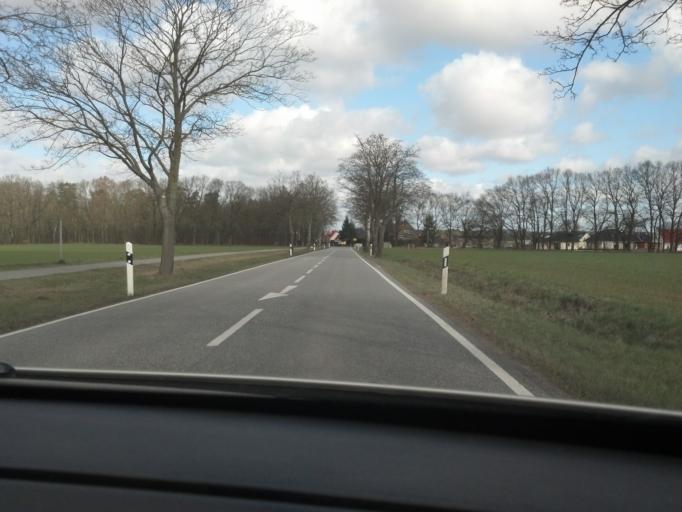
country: DE
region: Mecklenburg-Vorpommern
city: Boizenburg
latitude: 53.3917
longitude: 10.7516
